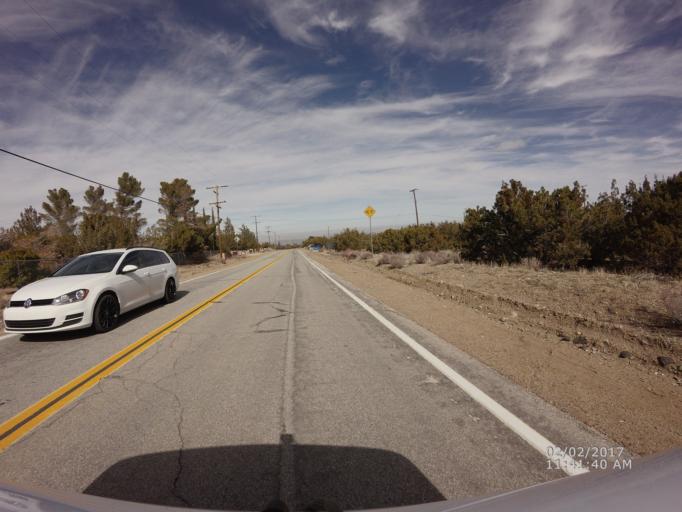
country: US
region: California
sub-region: Los Angeles County
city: Littlerock
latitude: 34.4477
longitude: -117.9359
